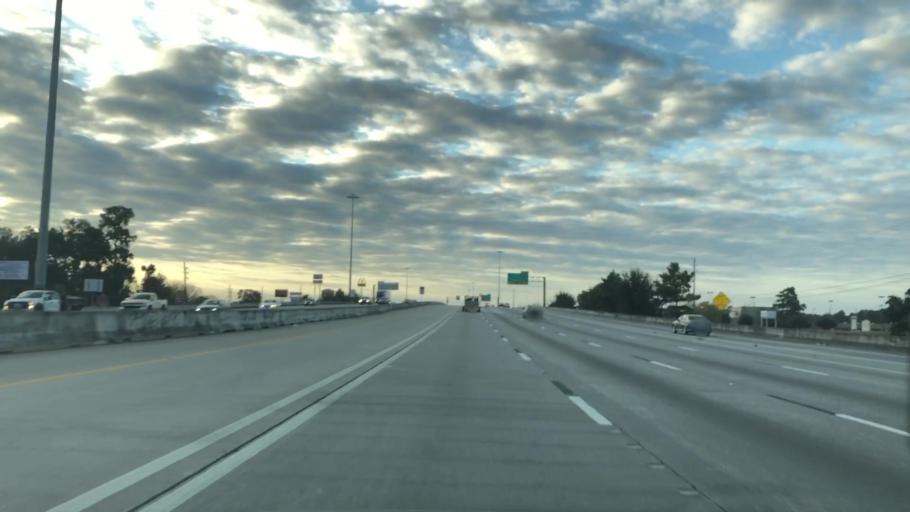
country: US
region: Texas
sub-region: Harris County
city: Spring
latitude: 30.0784
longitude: -95.4368
